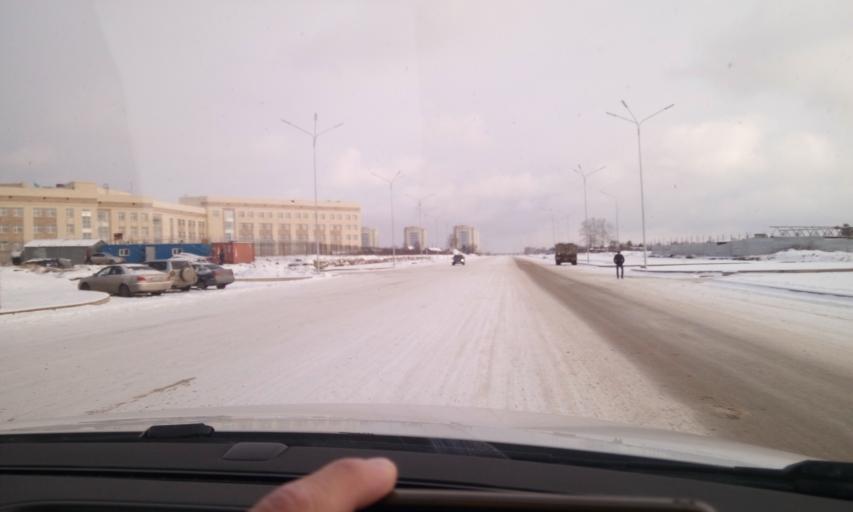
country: KZ
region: Astana Qalasy
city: Astana
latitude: 51.1211
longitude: 71.4923
